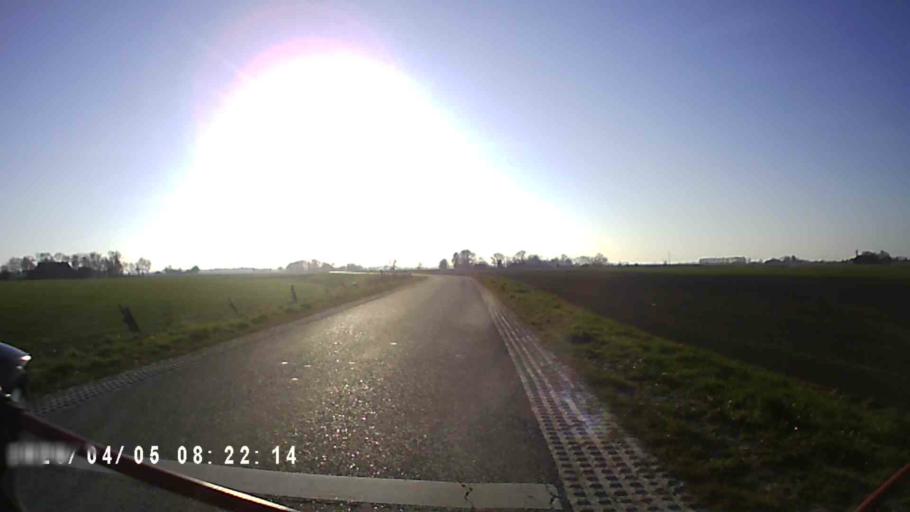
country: NL
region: Groningen
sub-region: Gemeente Zuidhorn
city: Oldehove
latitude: 53.3317
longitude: 6.4539
